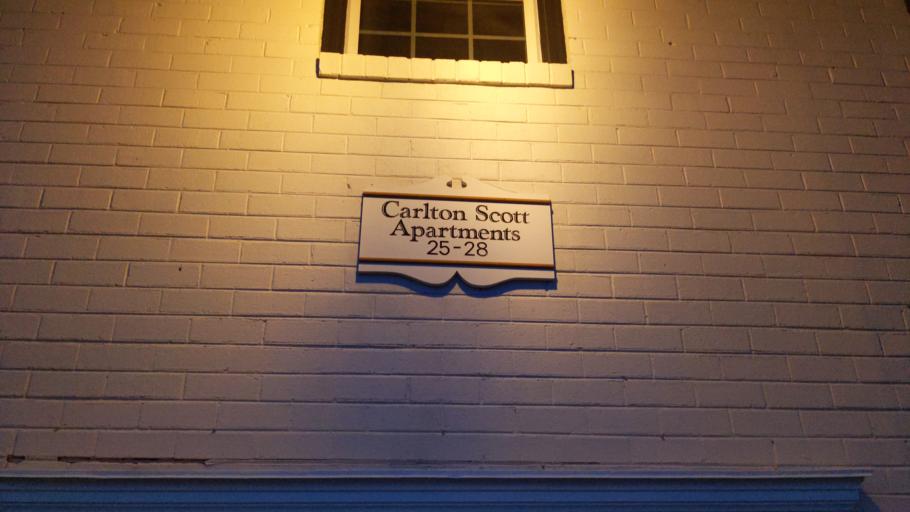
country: US
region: Virginia
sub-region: Montgomery County
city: Blacksburg
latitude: 37.2418
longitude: -80.4280
